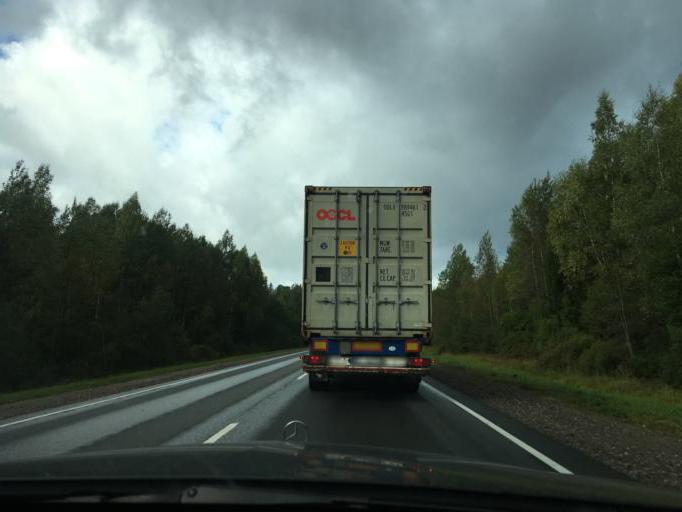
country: RU
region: Tverskaya
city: Nelidovo
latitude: 56.2660
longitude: 32.8161
